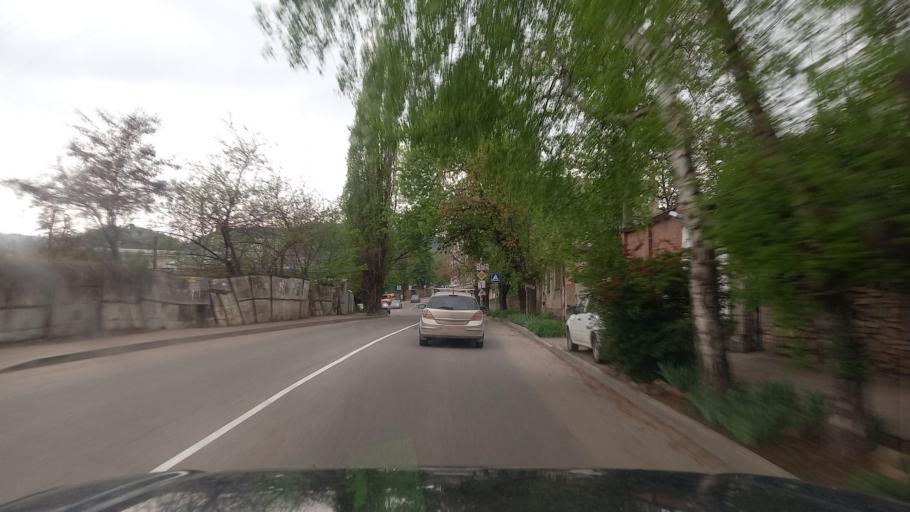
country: RU
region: Stavropol'skiy
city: Kislovodsk
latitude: 43.8996
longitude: 42.7118
